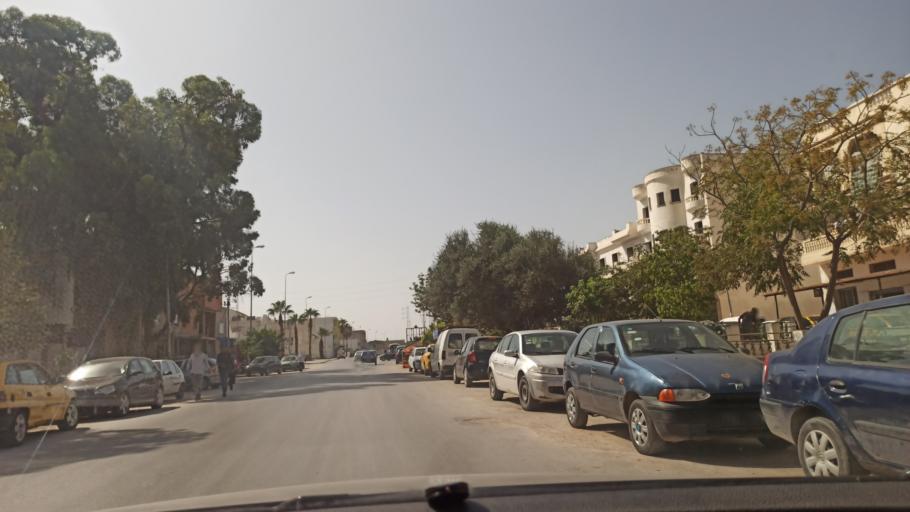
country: TN
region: Manouba
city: Manouba
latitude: 36.7658
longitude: 10.1108
